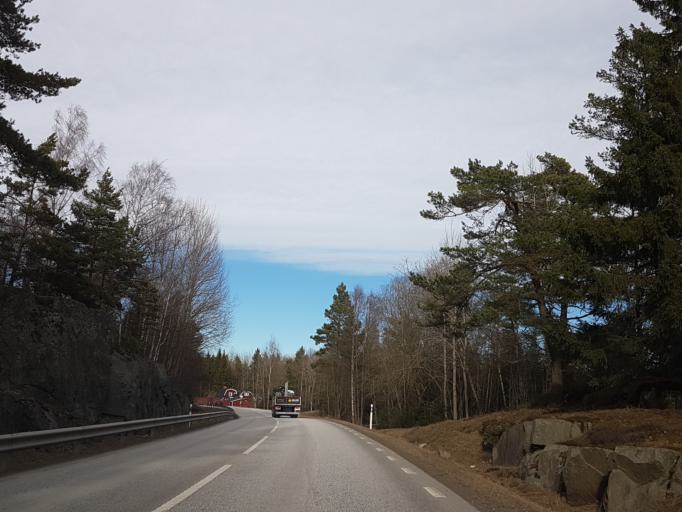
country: SE
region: Stockholm
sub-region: Norrtalje Kommun
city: Norrtalje
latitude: 59.7240
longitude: 18.6759
